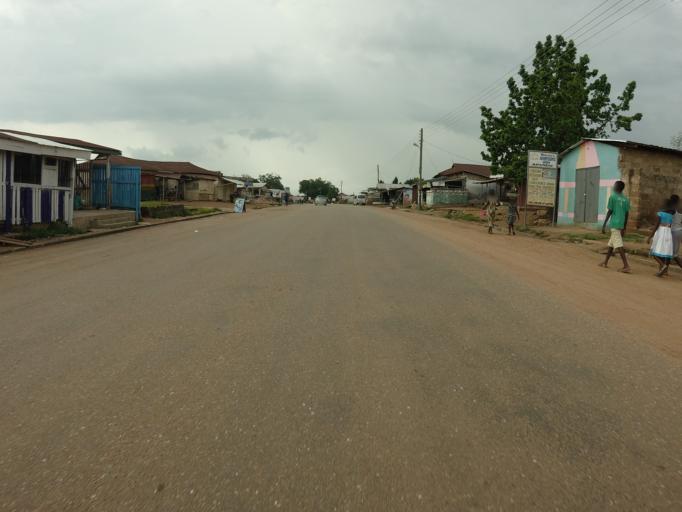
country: GH
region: Volta
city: Kpandu
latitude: 6.9986
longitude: 0.4382
